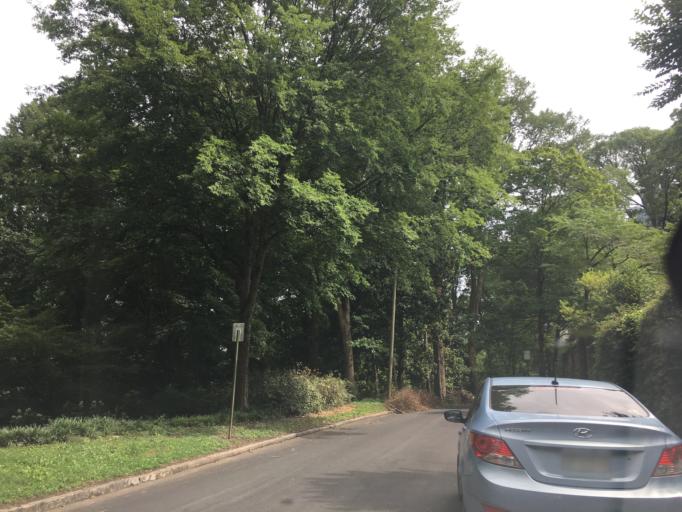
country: US
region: Georgia
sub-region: Fulton County
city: Atlanta
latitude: 33.7899
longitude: -84.3808
